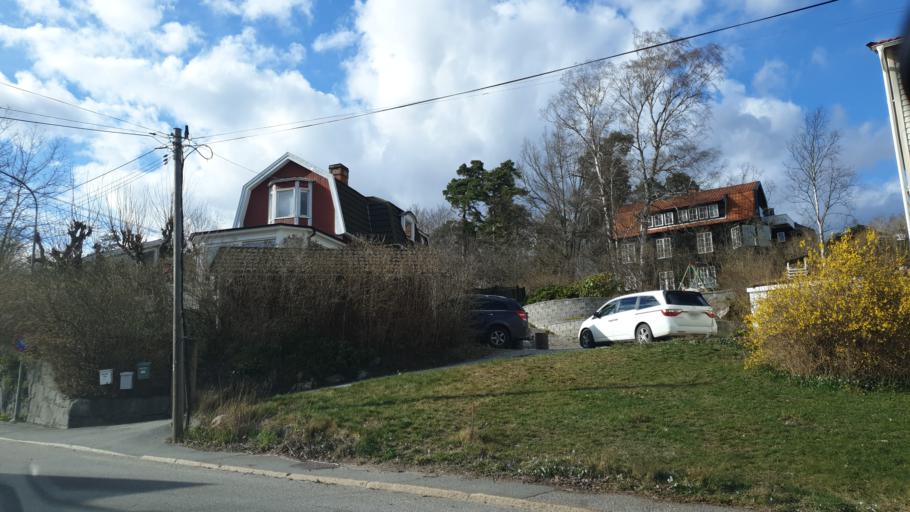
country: SE
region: Stockholm
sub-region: Nacka Kommun
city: Alta
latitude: 59.3009
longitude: 18.2020
